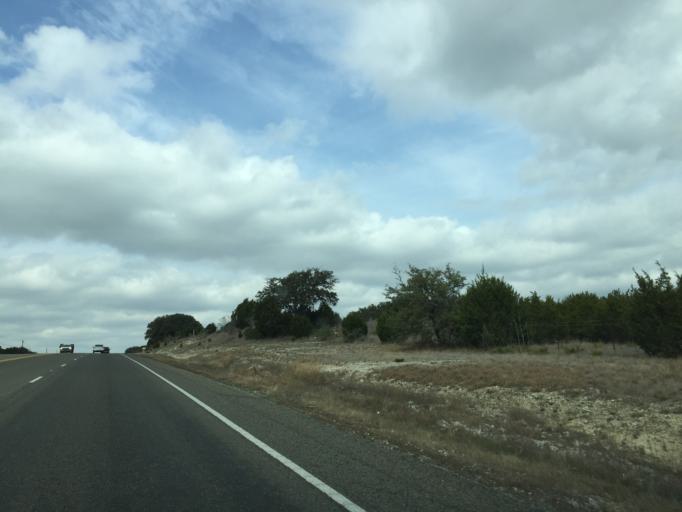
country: US
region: Texas
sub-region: Travis County
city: Briarcliff
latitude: 30.4277
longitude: -98.1360
